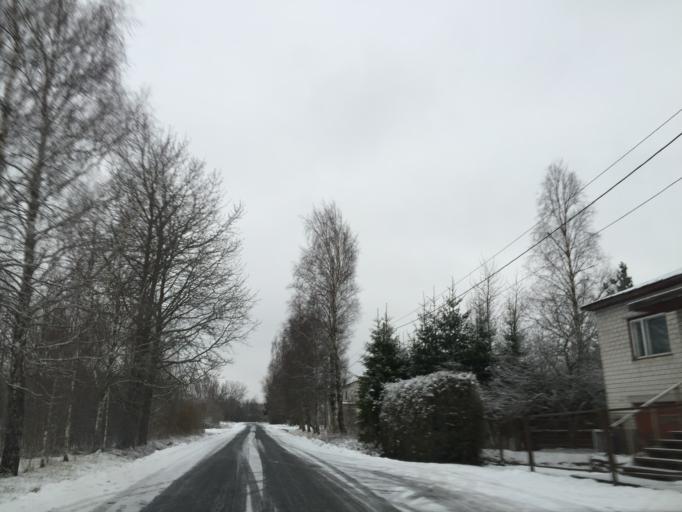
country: EE
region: Laeaene
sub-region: Lihula vald
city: Lihula
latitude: 58.6817
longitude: 23.8358
